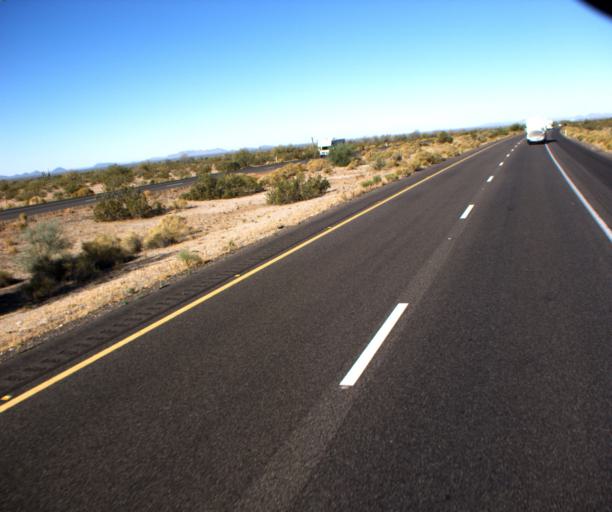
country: US
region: Arizona
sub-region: Maricopa County
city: Gila Bend
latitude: 32.9059
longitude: -112.5797
